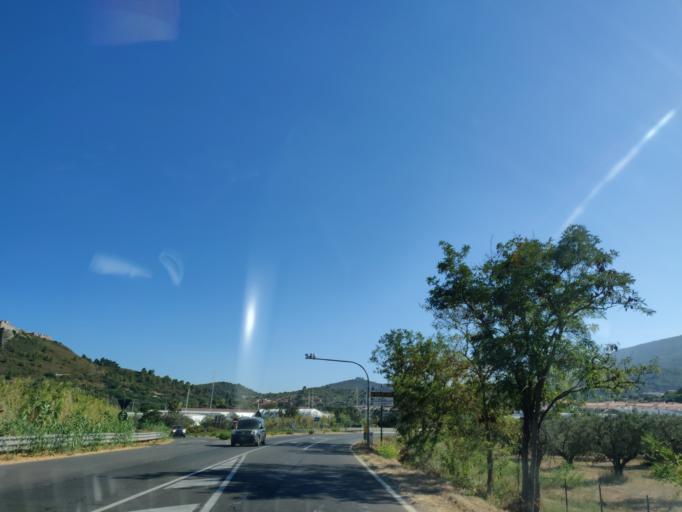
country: IT
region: Tuscany
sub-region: Provincia di Grosseto
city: Porto Ercole
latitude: 42.4049
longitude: 11.2004
